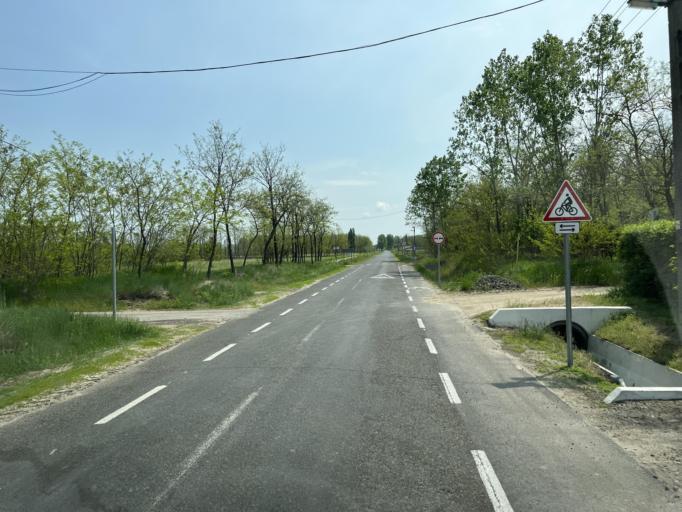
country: HU
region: Pest
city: Nagykoros
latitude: 47.0991
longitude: 19.8094
